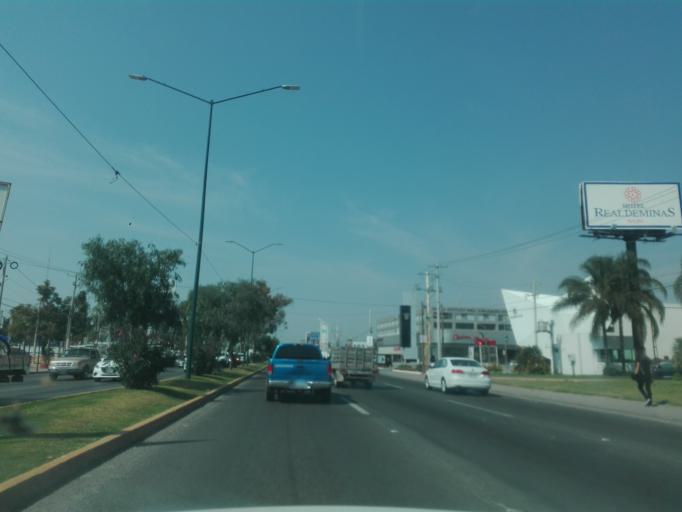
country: MX
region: Guanajuato
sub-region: Leon
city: Fraccionamiento Paraiso Real
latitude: 21.0835
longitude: -101.6122
